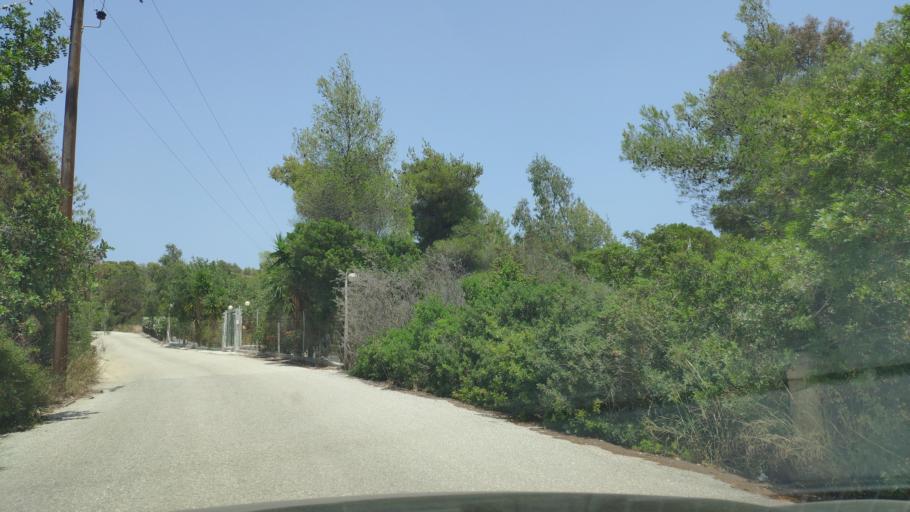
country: GR
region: Peloponnese
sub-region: Nomos Argolidos
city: Porto Cheli
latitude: 37.3069
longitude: 23.1463
